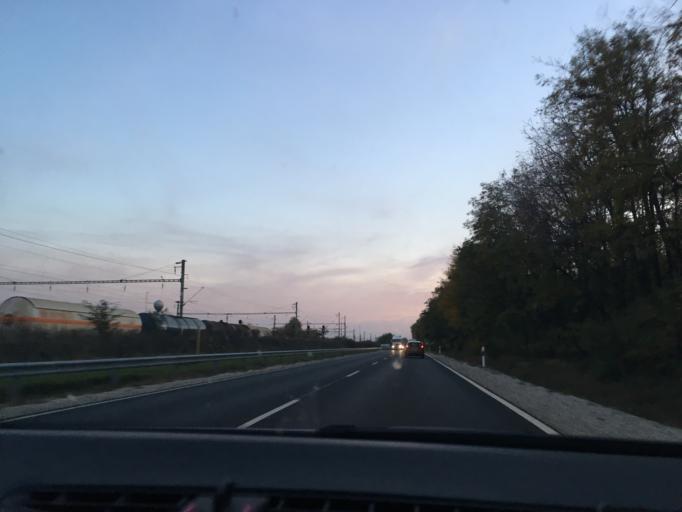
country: HU
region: Hajdu-Bihar
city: Debrecen
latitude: 47.5810
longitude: 21.6548
